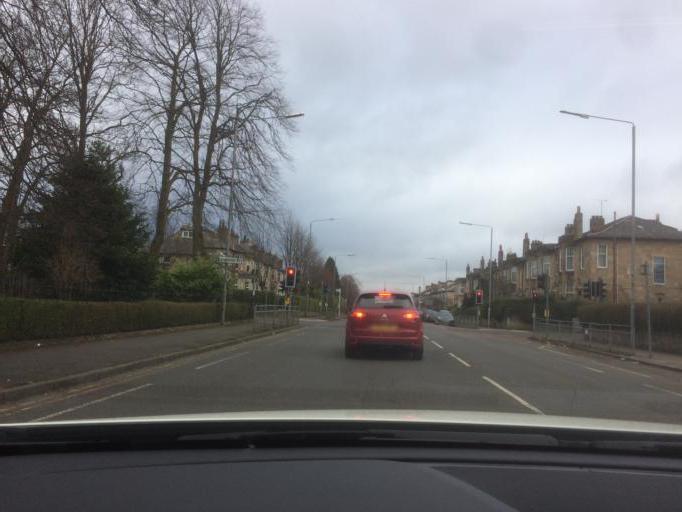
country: GB
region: Scotland
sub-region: East Renfrewshire
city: Giffnock
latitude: 55.8217
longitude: -4.2869
